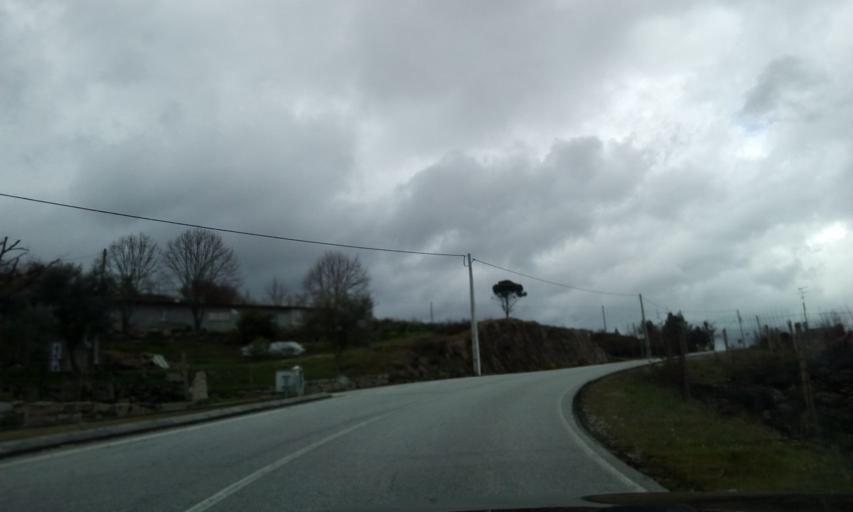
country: PT
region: Viseu
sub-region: Viseu
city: Rio de Loba
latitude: 40.6102
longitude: -7.8651
